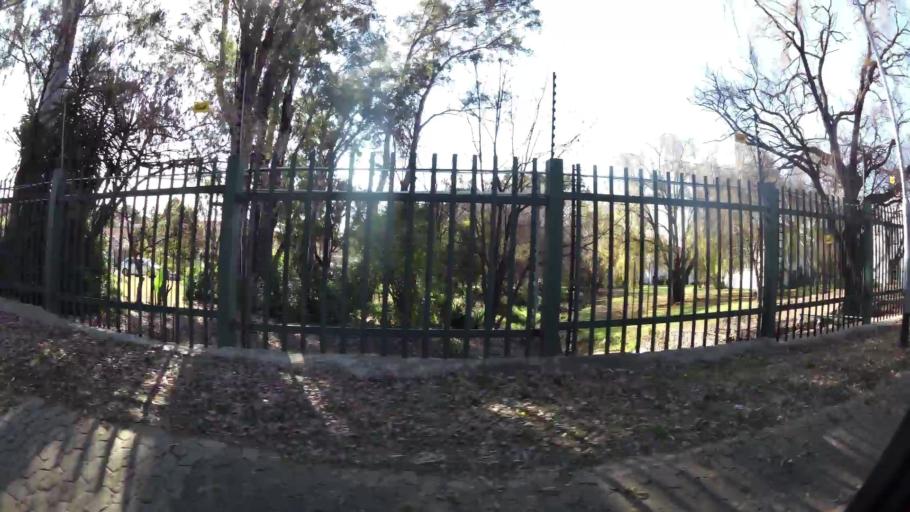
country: ZA
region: Gauteng
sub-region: City of Johannesburg Metropolitan Municipality
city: Roodepoort
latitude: -26.1194
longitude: 27.9605
